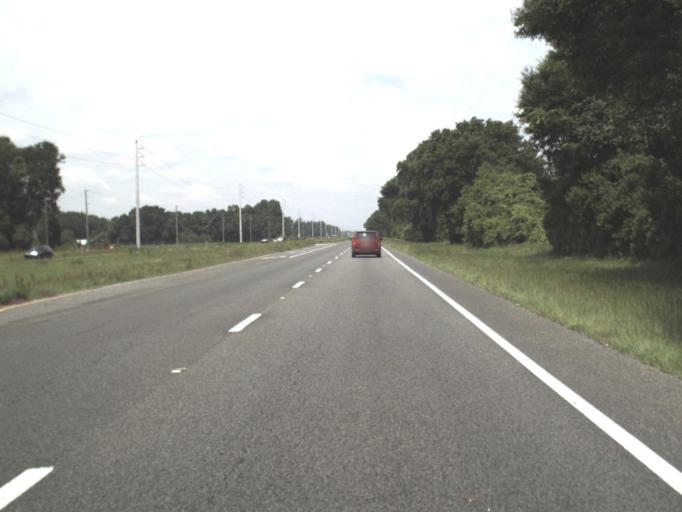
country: US
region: Florida
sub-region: Levy County
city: Chiefland
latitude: 29.4751
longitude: -82.7957
